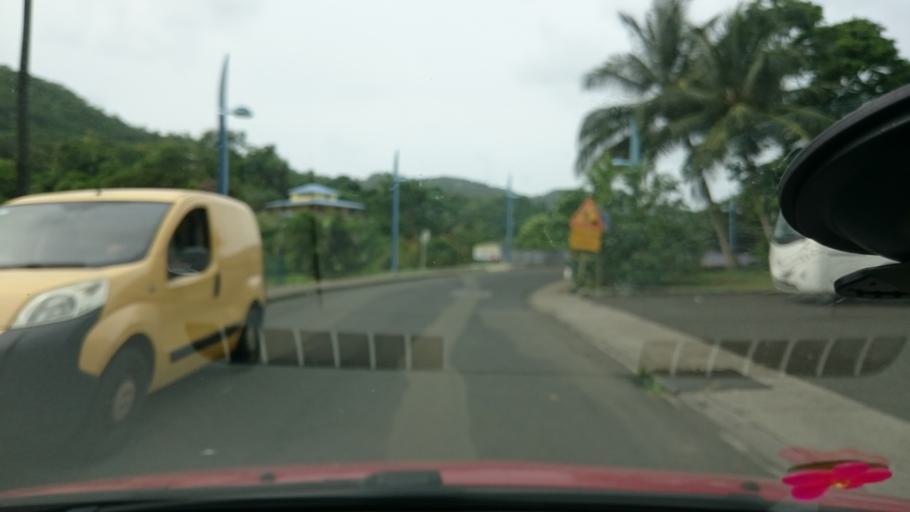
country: MQ
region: Martinique
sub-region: Martinique
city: Riviere-Pilote
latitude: 14.4857
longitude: -60.9040
